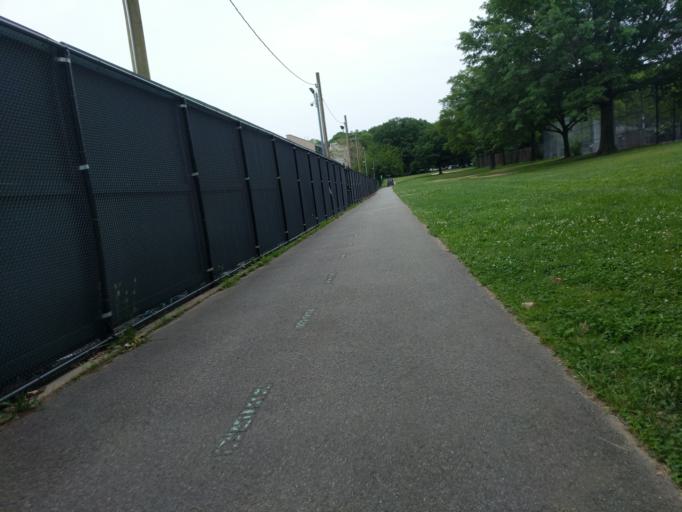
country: US
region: New York
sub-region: Nassau County
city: Bellerose Terrace
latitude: 40.7422
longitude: -73.7776
